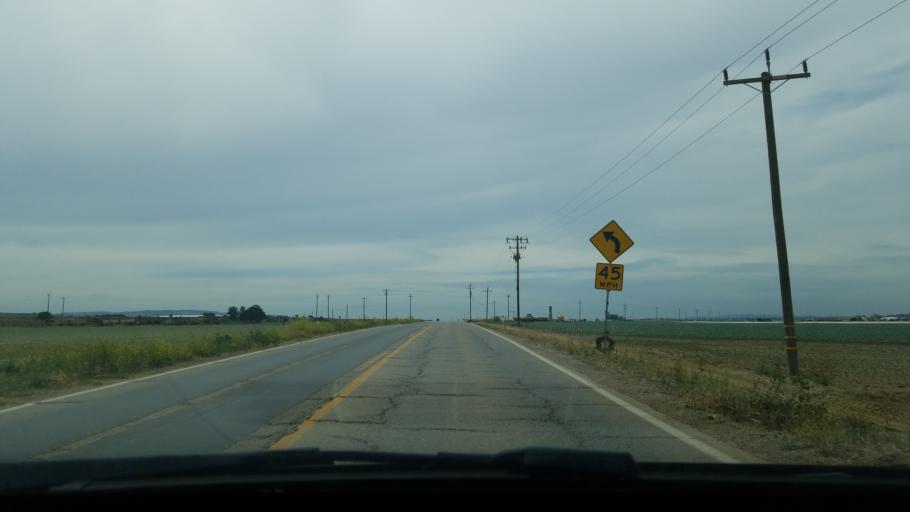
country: US
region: California
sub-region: Santa Barbara County
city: Orcutt
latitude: 34.9079
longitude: -120.3271
